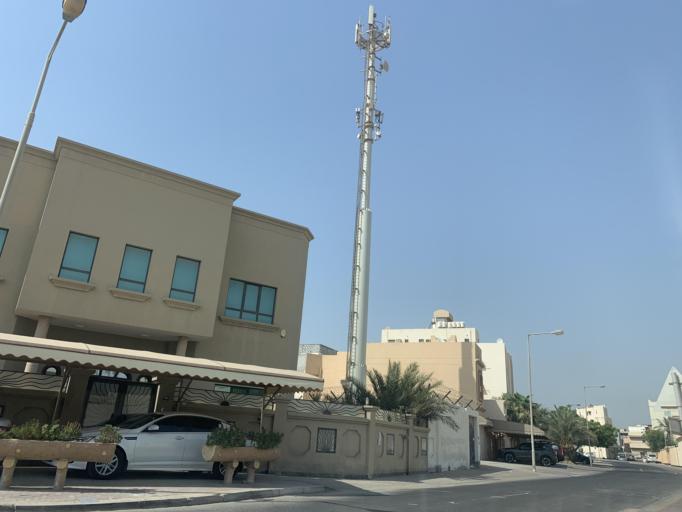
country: BH
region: Manama
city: Jidd Hafs
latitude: 26.2045
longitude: 50.5283
